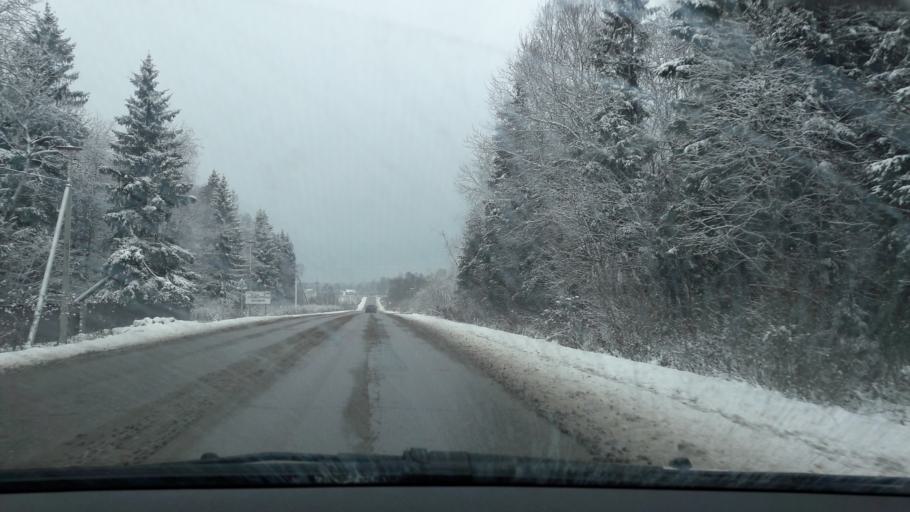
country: RU
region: Moskovskaya
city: Zvenigorod
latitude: 55.6294
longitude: 36.8629
